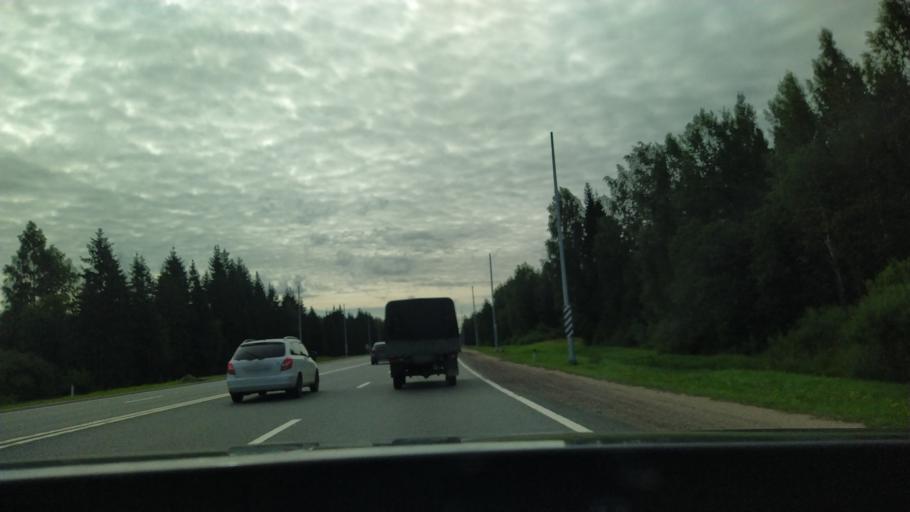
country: RU
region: Leningrad
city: Ul'yanovka
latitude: 59.5911
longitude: 30.7858
